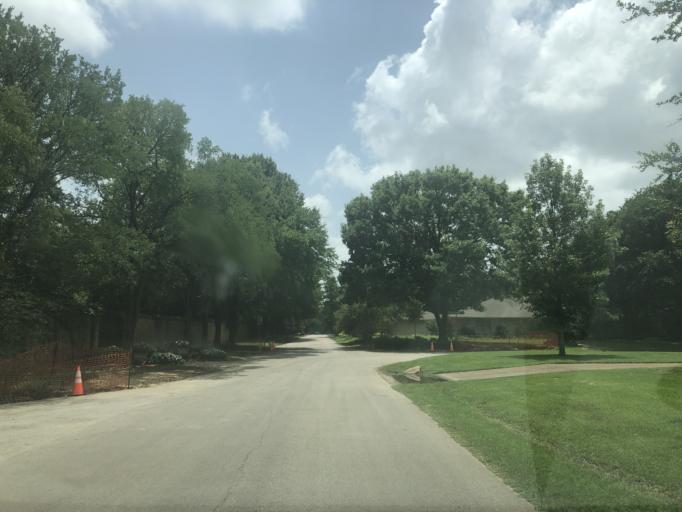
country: US
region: Texas
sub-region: Dallas County
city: University Park
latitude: 32.8771
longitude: -96.8347
